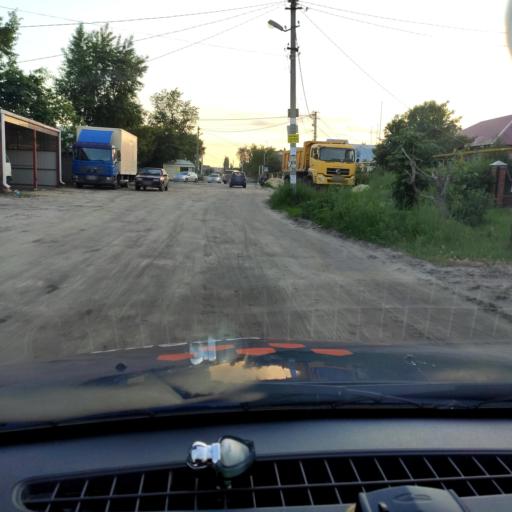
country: RU
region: Voronezj
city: Somovo
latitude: 51.7456
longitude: 39.3408
